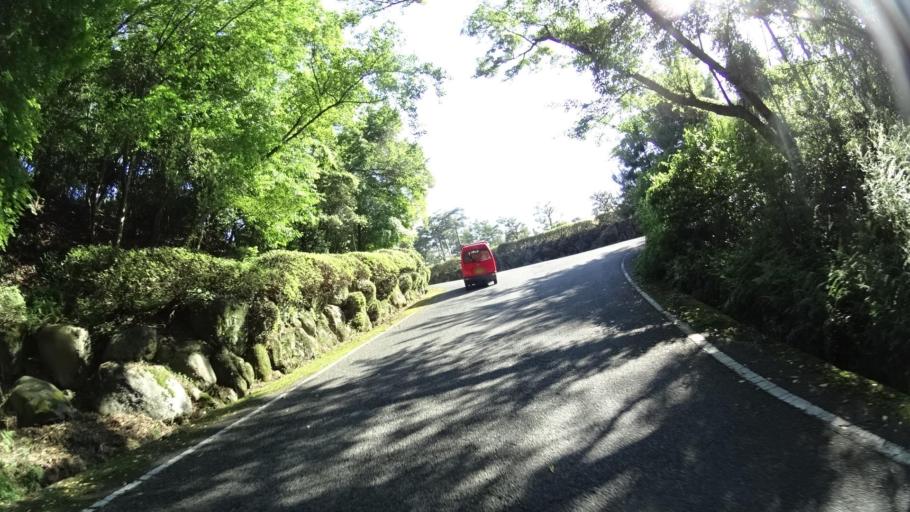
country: JP
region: Kyoto
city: Kameoka
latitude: 34.9919
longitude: 135.5631
